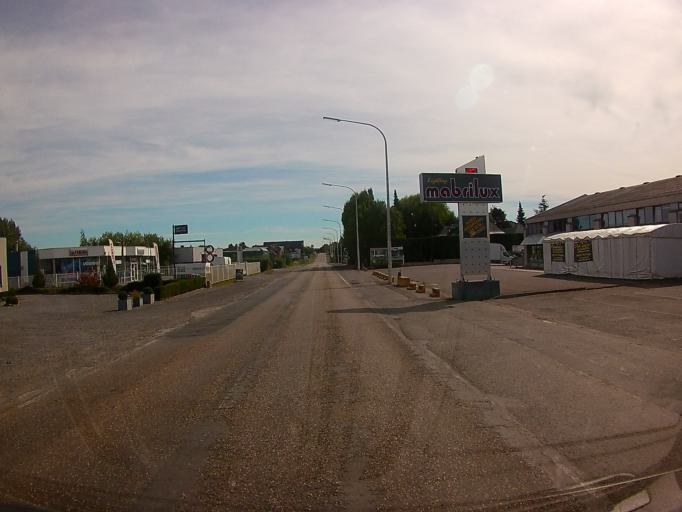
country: BE
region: Wallonia
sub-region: Province de Liege
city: Welkenraedt
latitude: 50.6738
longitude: 5.9690
